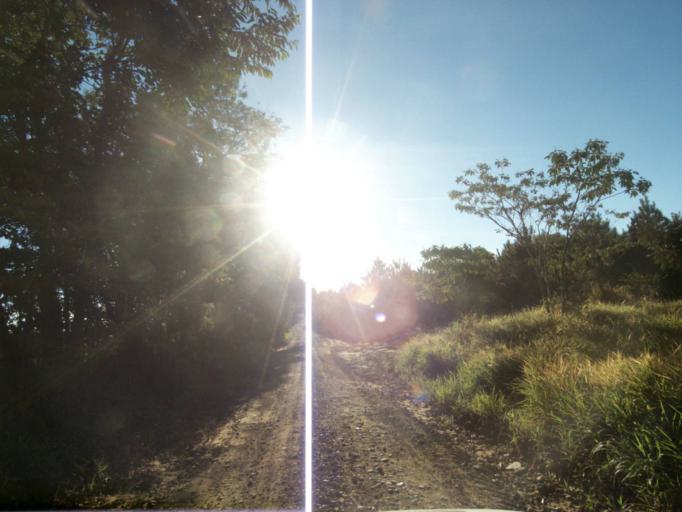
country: BR
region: Parana
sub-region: Tibagi
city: Tibagi
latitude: -24.5195
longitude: -50.5978
